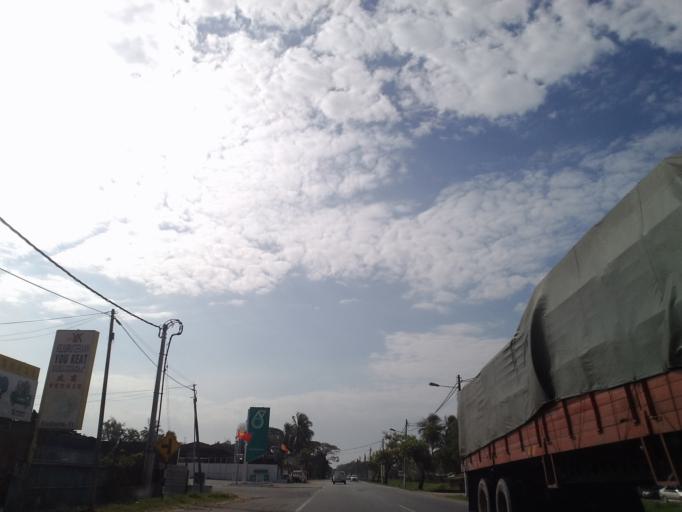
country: MY
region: Kedah
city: Alor Setar
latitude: 6.0485
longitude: 100.3732
